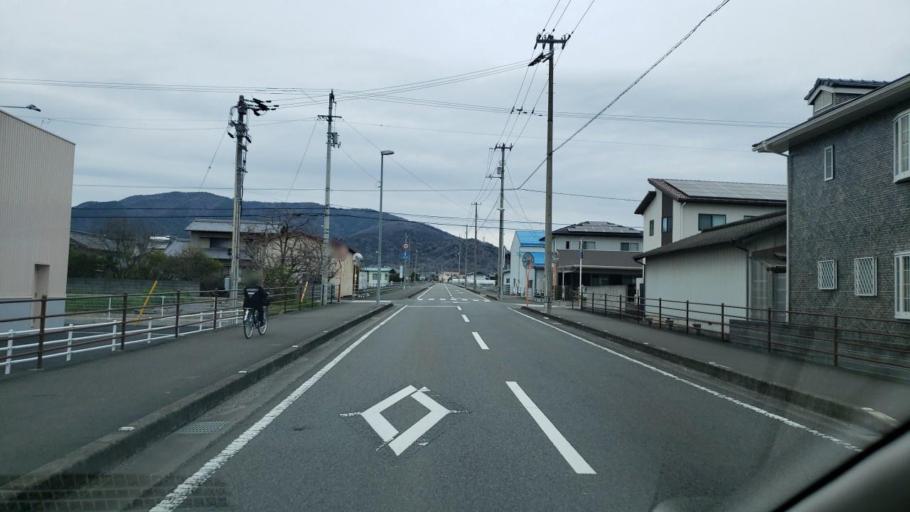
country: JP
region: Tokushima
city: Kamojimacho-jogejima
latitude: 34.1023
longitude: 134.3413
